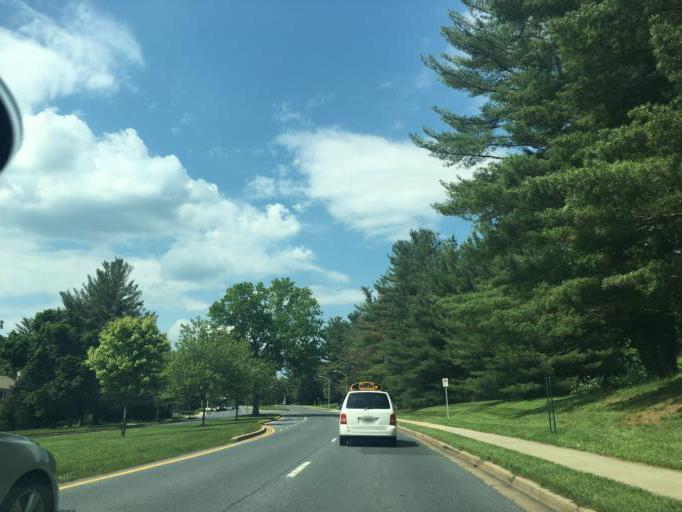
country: US
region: Maryland
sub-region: Montgomery County
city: Montgomery Village
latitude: 39.1822
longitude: -77.1993
